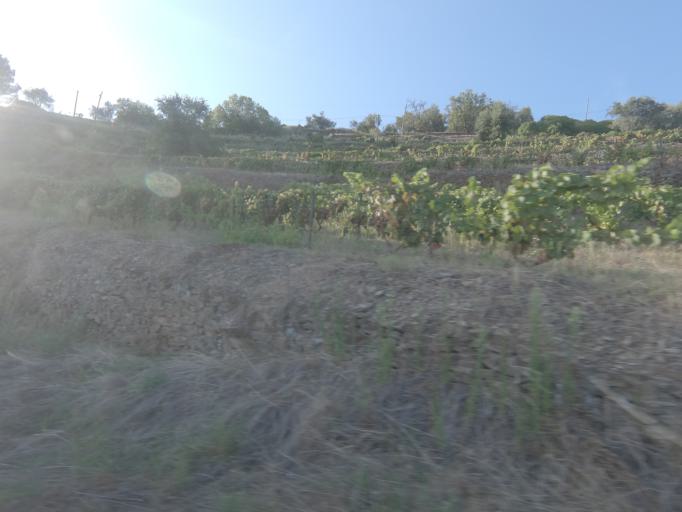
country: PT
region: Vila Real
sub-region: Sabrosa
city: Sabrosa
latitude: 41.2646
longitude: -7.5384
